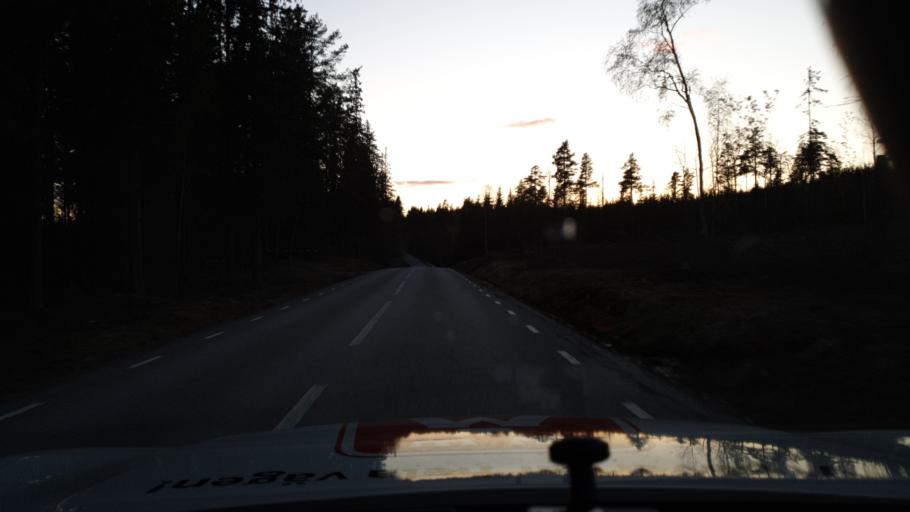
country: SE
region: OErebro
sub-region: Lindesbergs Kommun
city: Stora
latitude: 59.8935
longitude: 15.2426
